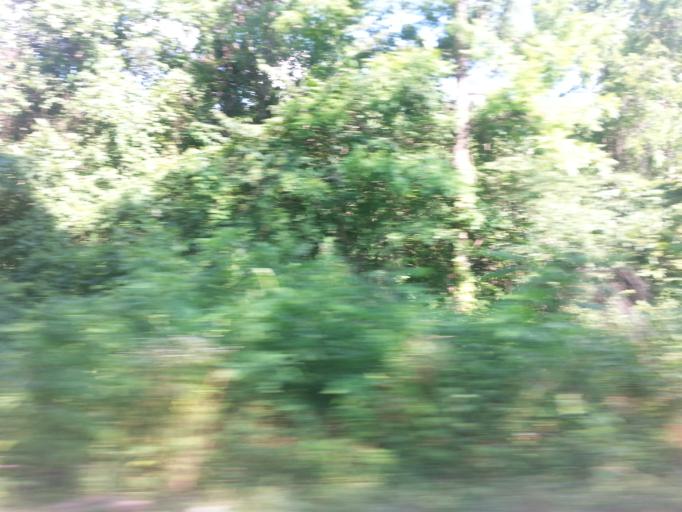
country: US
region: Tennessee
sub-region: Knox County
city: Knoxville
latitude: 36.0838
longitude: -83.8990
